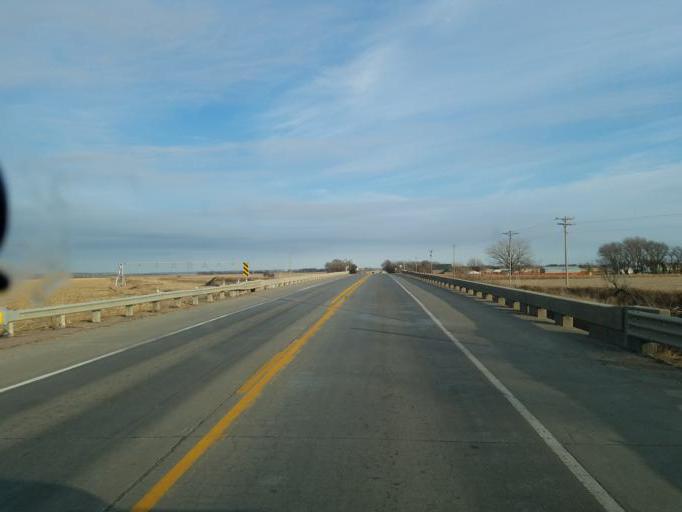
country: US
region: South Dakota
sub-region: Union County
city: Dakota Dunes
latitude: 42.4483
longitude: -96.5588
